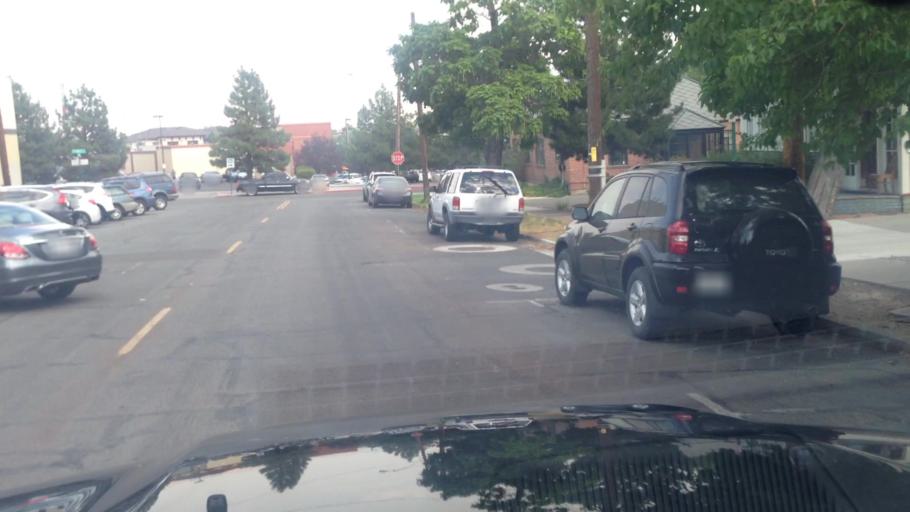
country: US
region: Nevada
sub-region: Washoe County
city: Reno
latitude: 39.5189
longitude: -119.8124
